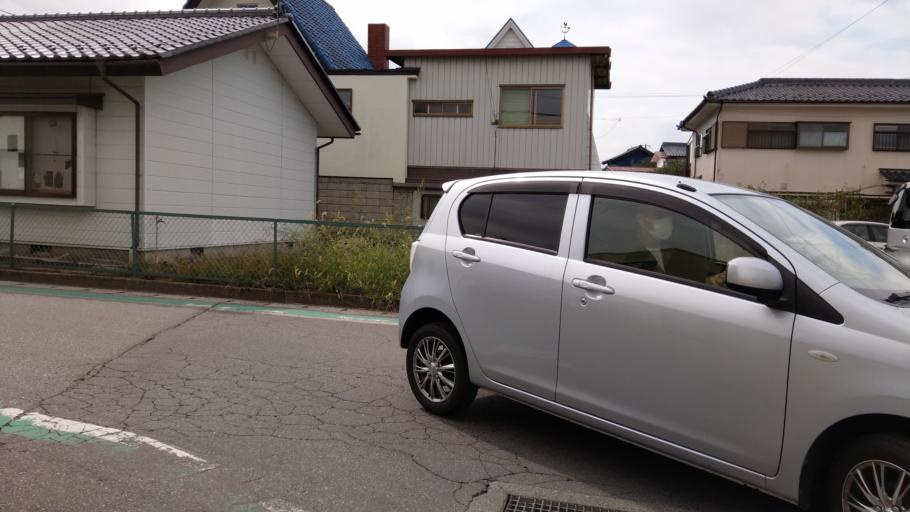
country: JP
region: Nagano
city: Saku
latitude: 36.2695
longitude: 138.4808
